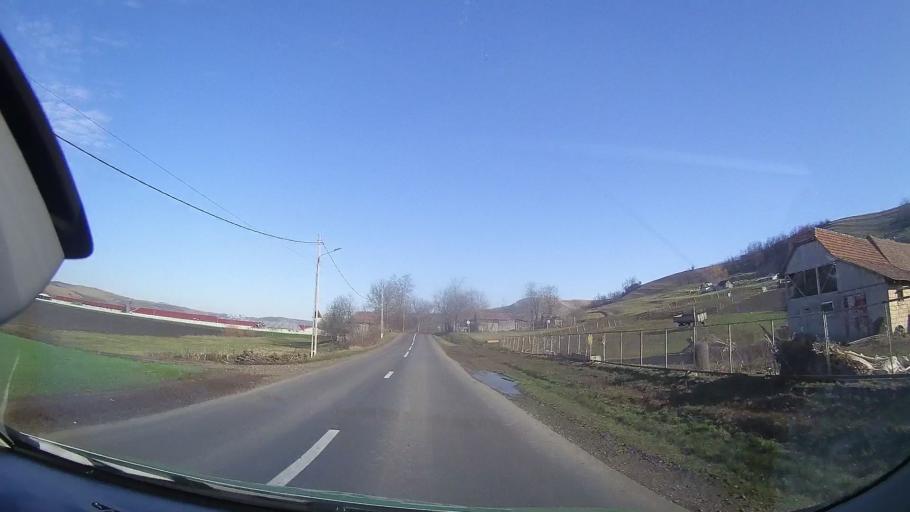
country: RO
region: Mures
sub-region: Comuna Iclanzel
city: Iclanzel
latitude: 46.5481
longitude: 24.3260
